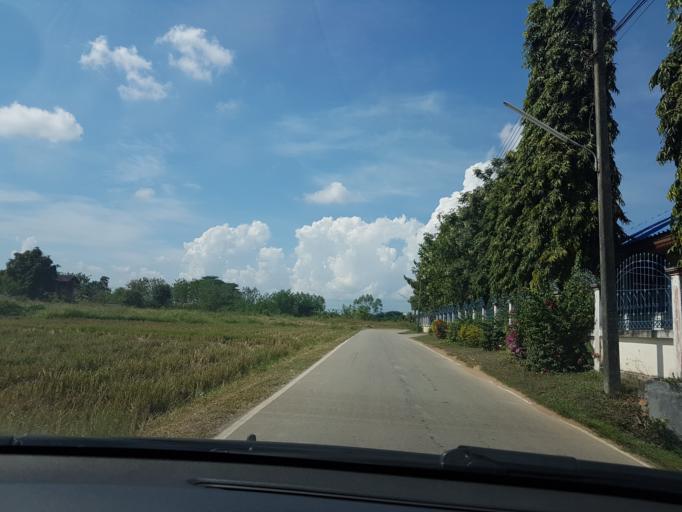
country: TH
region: Lampang
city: Ko Kha
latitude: 18.2091
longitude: 99.3985
